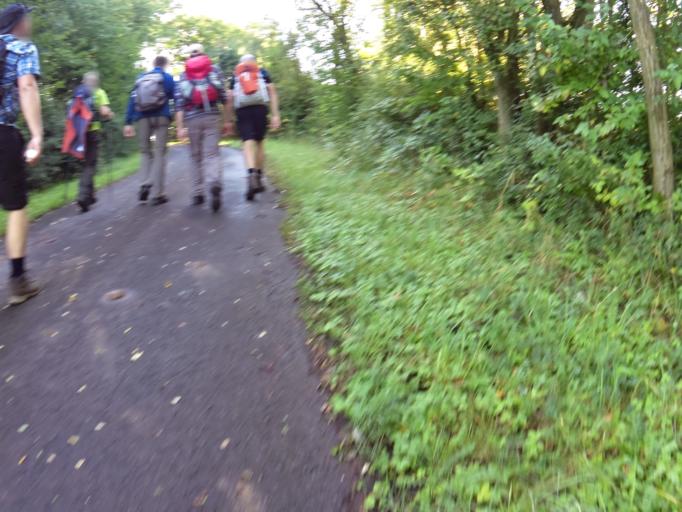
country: DE
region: Rheinland-Pfalz
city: Waldbockelheim
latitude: 49.8114
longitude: 7.7260
